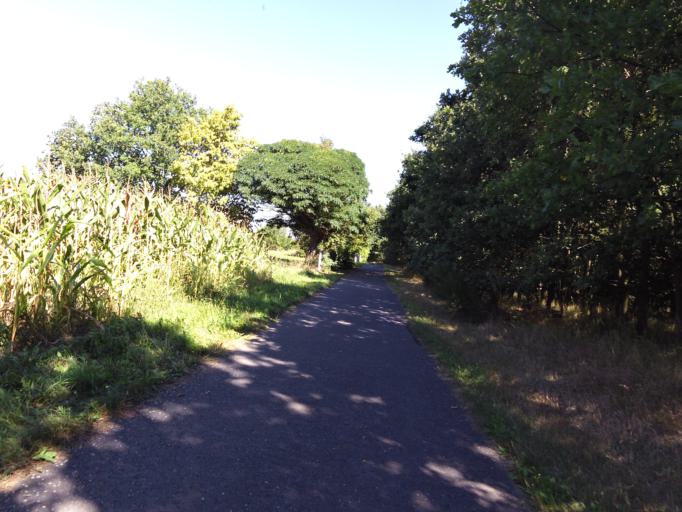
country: DE
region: Saxony-Anhalt
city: Pretzsch
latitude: 51.6911
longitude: 12.8274
